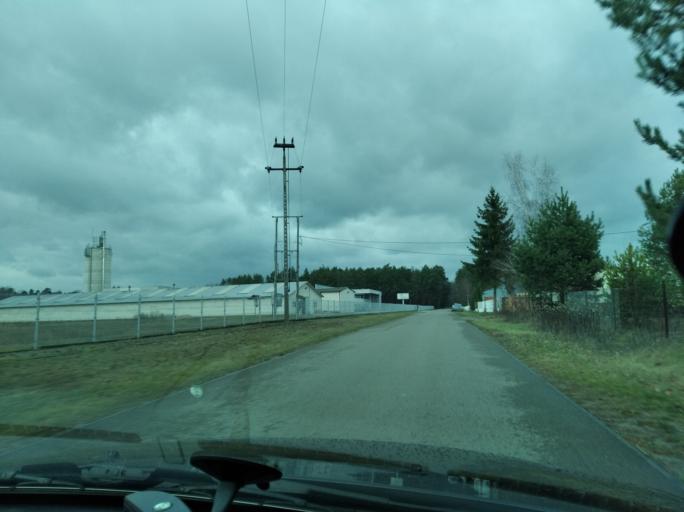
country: PL
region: Subcarpathian Voivodeship
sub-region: Powiat lancucki
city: Zolynia
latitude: 50.1347
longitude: 22.2829
